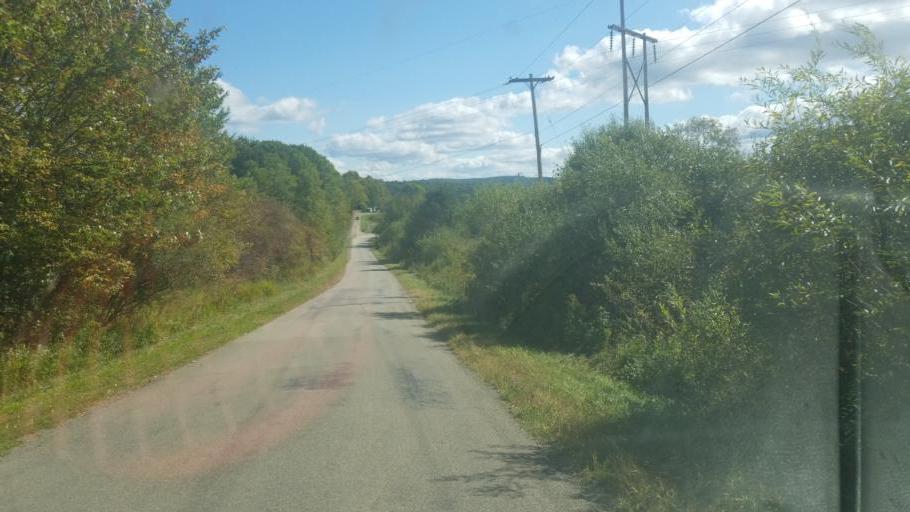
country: US
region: New York
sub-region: Allegany County
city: Cuba
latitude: 42.1706
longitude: -78.3492
